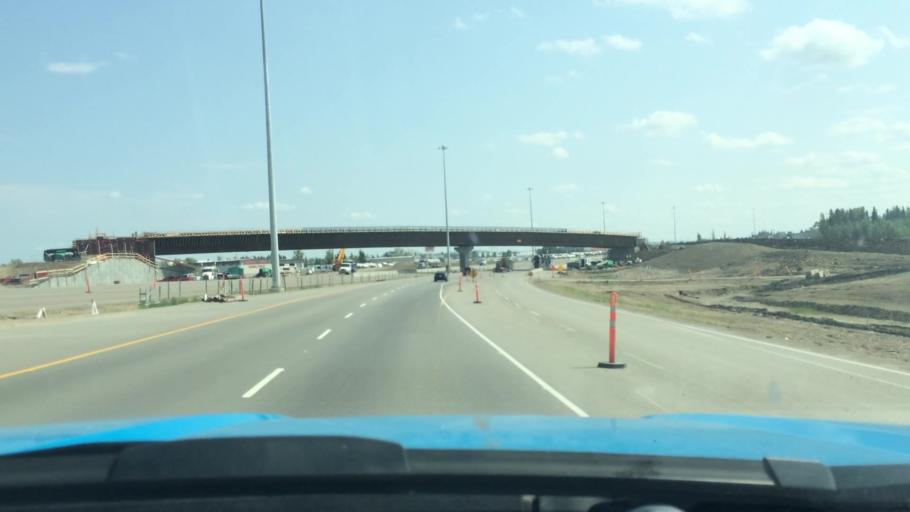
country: CA
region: Alberta
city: Red Deer
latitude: 52.2292
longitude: -113.8179
